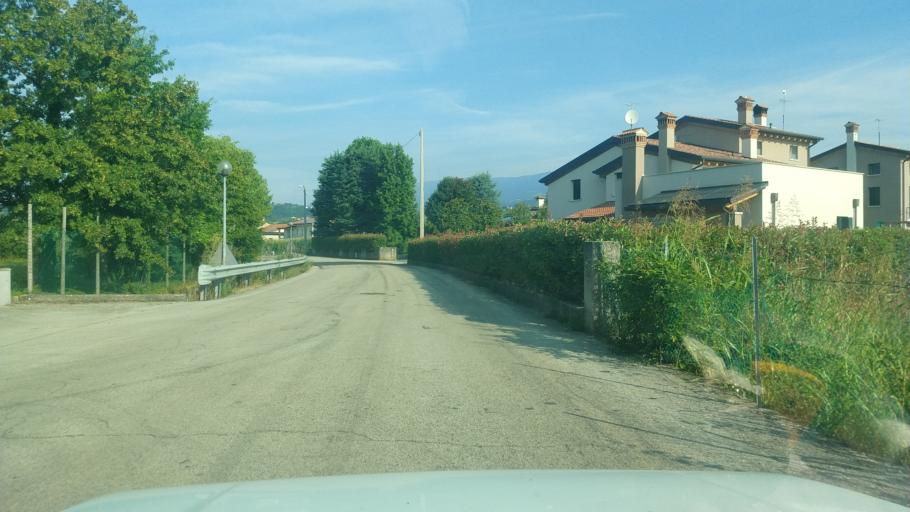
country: IT
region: Veneto
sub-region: Provincia di Vicenza
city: Mason Vicentino
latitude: 45.7220
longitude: 11.6219
